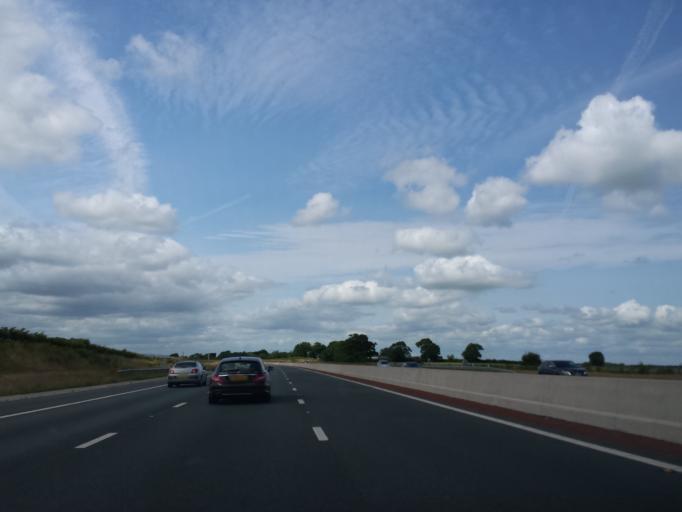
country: GB
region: England
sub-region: North Yorkshire
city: Bedale
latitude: 54.2746
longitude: -1.5286
